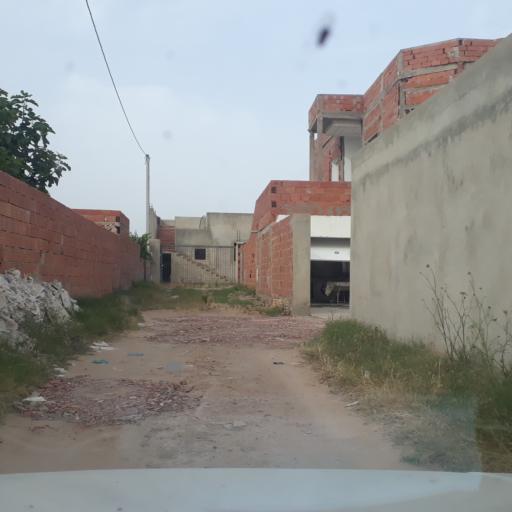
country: TN
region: Safaqis
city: Al Qarmadah
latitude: 34.8221
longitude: 10.7742
